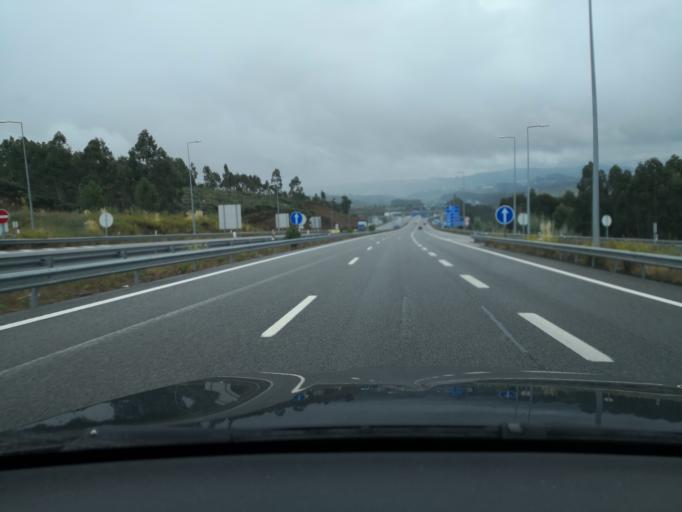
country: PT
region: Porto
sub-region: Valongo
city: Sobrado
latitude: 41.2327
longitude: -8.4680
